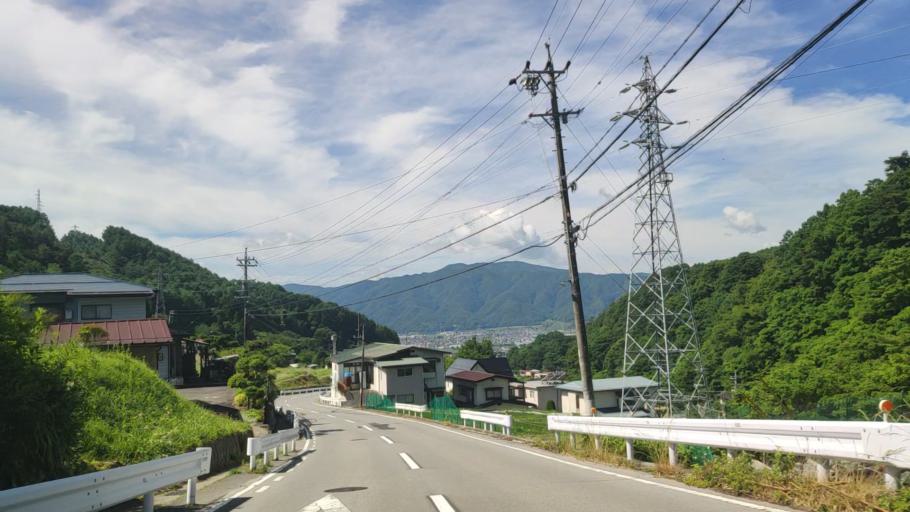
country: JP
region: Nagano
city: Suwa
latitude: 36.0568
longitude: 138.1298
